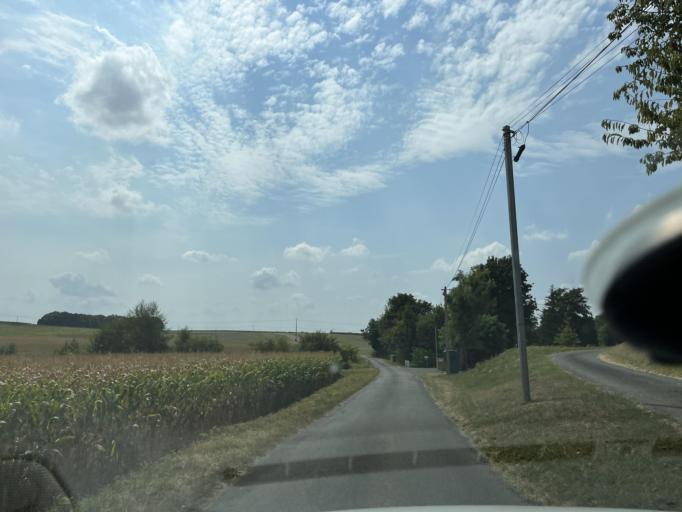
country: FR
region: Poitou-Charentes
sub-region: Departement de la Charente-Maritime
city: Pons
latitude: 45.5904
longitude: -0.5741
